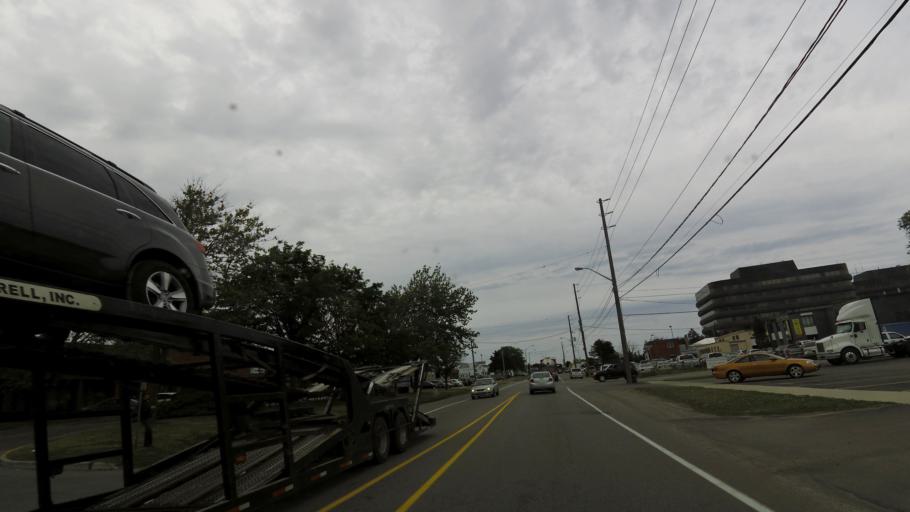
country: CA
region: Ontario
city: Oakville
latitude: 43.4427
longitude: -79.7001
